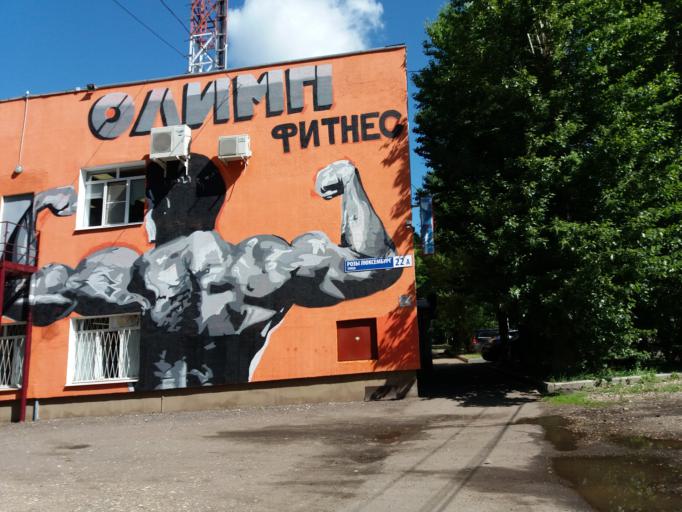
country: RU
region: Jaroslavl
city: Yaroslavl
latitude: 57.6389
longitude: 39.8346
